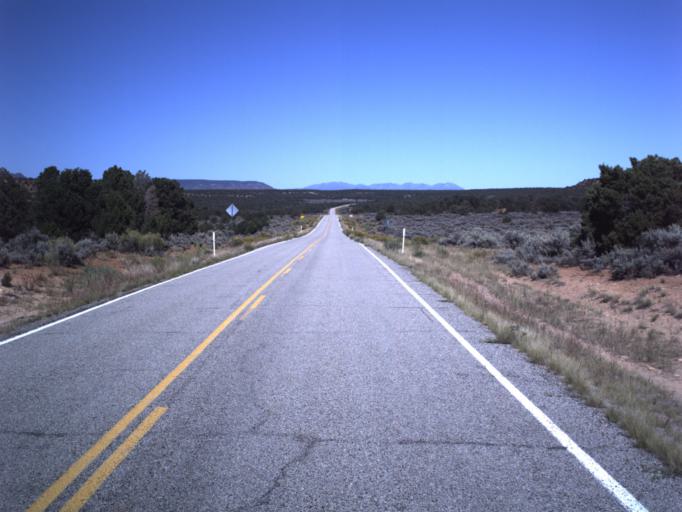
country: US
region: Utah
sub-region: San Juan County
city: Blanding
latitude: 37.4215
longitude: -109.9423
